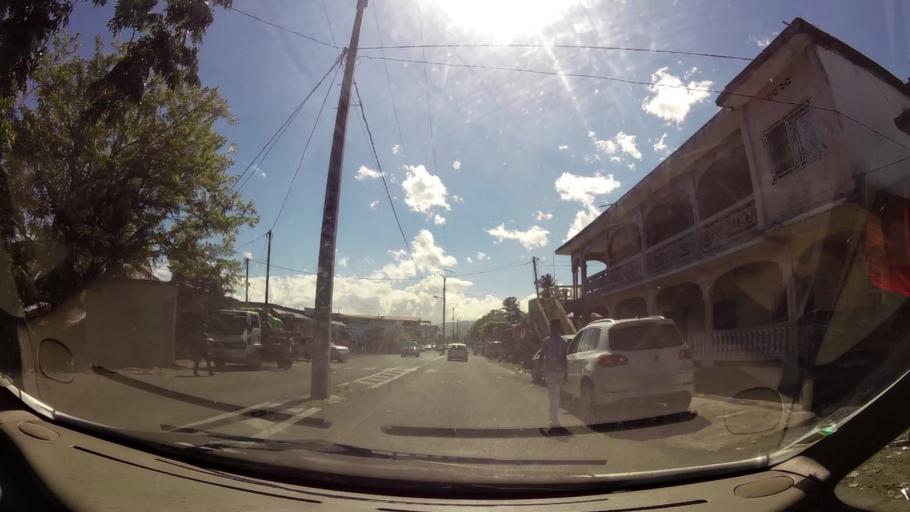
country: KM
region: Grande Comore
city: Tsidje
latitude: -11.6971
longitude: 43.2569
